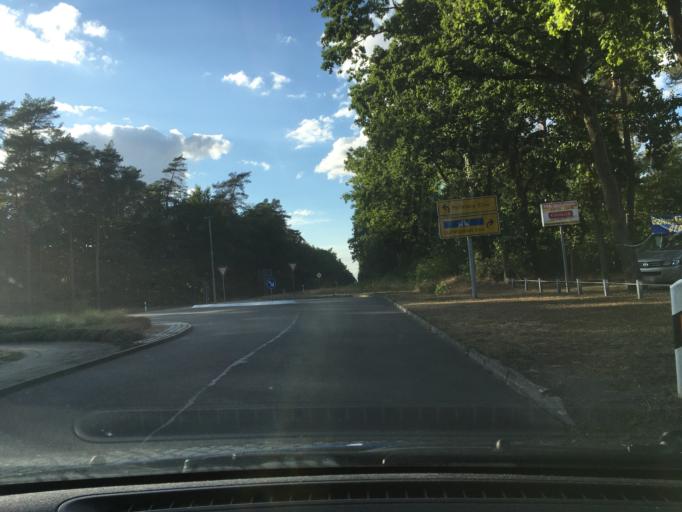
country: DE
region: Mecklenburg-Vorpommern
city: Grabow
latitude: 53.2860
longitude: 11.5533
